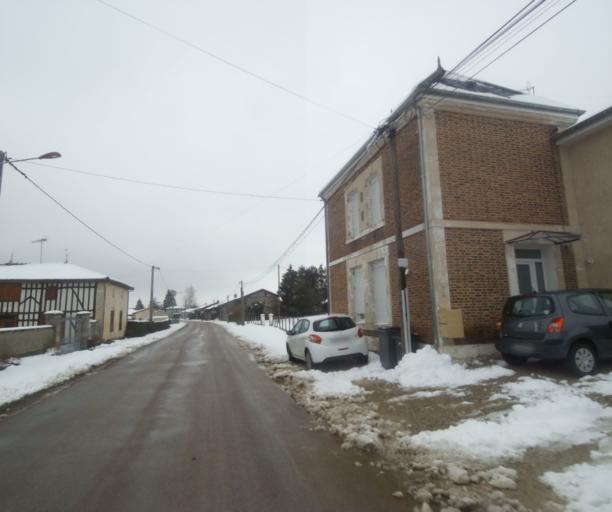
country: FR
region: Champagne-Ardenne
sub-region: Departement de la Haute-Marne
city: Laneuville-a-Remy
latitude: 48.5068
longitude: 4.8585
